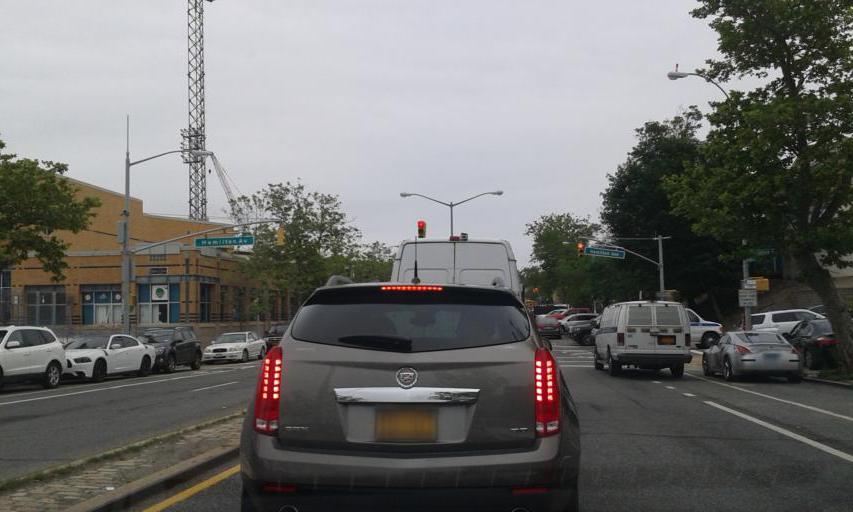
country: US
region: New Jersey
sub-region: Hudson County
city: Bayonne
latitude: 40.6458
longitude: -74.0780
